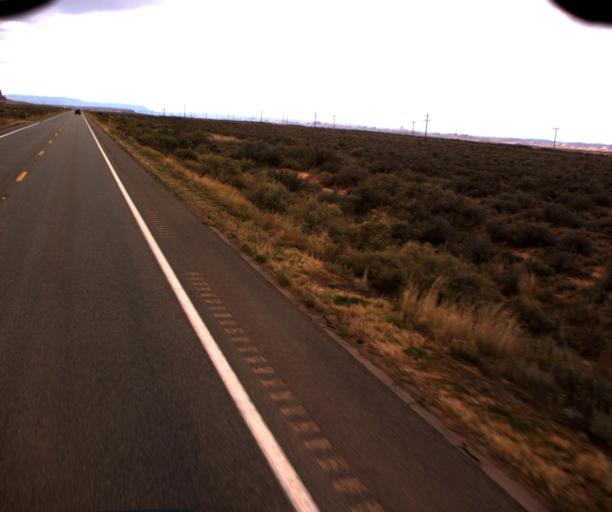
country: US
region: Arizona
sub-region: Navajo County
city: Kayenta
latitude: 36.8173
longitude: -109.8843
